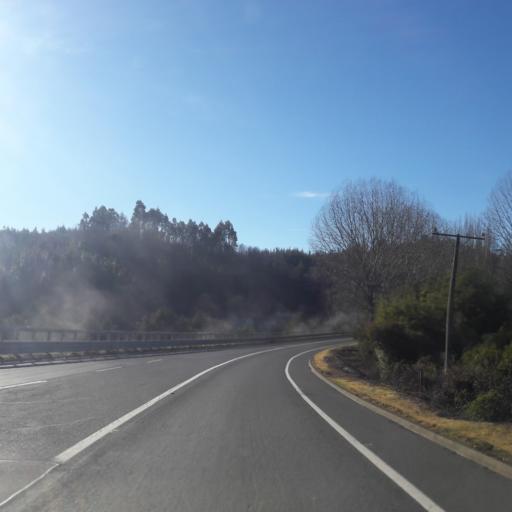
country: CL
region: Biobio
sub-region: Provincia de Biobio
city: La Laja
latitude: -37.2727
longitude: -72.9526
